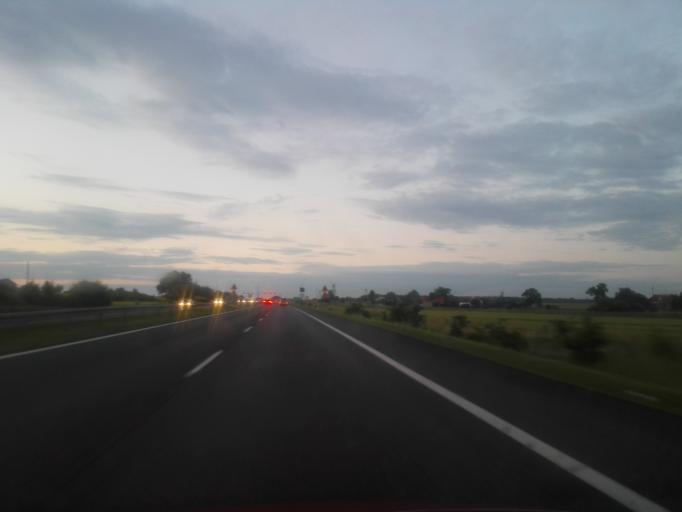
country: PL
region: Lodz Voivodeship
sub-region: Powiat piotrkowski
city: Wola Krzysztoporska
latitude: 51.3185
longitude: 19.5767
